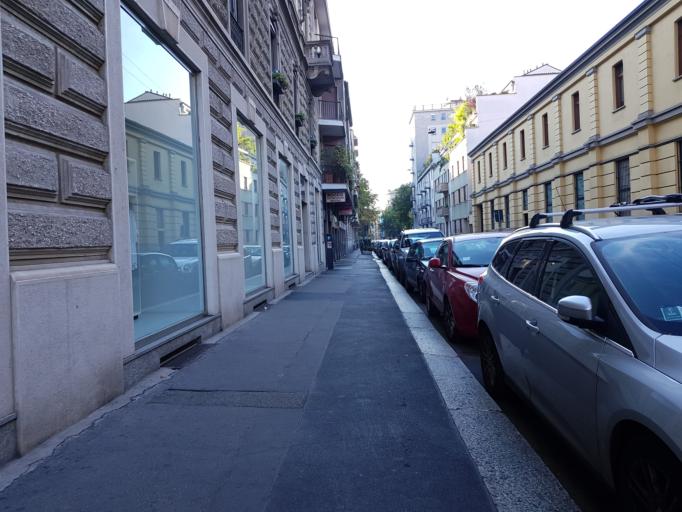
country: IT
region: Lombardy
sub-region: Citta metropolitana di Milano
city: Milano
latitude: 45.4814
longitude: 9.2122
